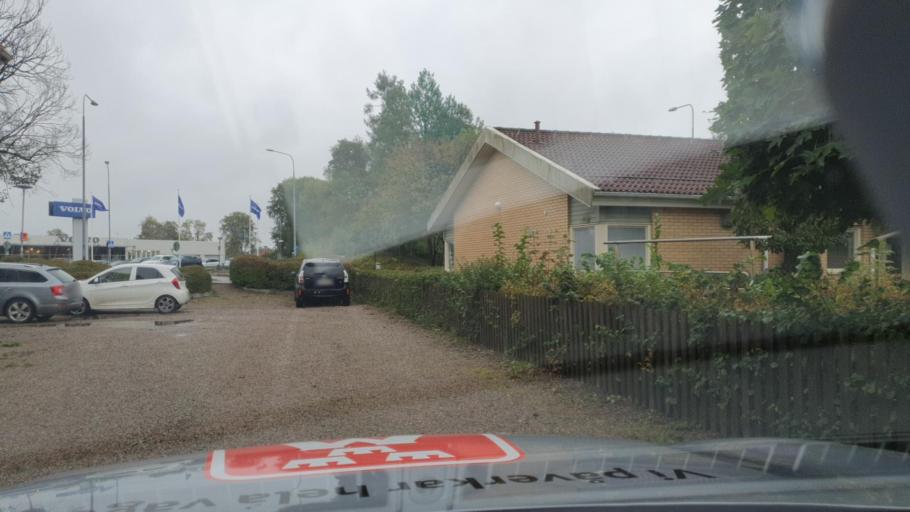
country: SE
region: Kronoberg
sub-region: Almhults Kommun
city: AElmhult
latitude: 56.5548
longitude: 14.1412
